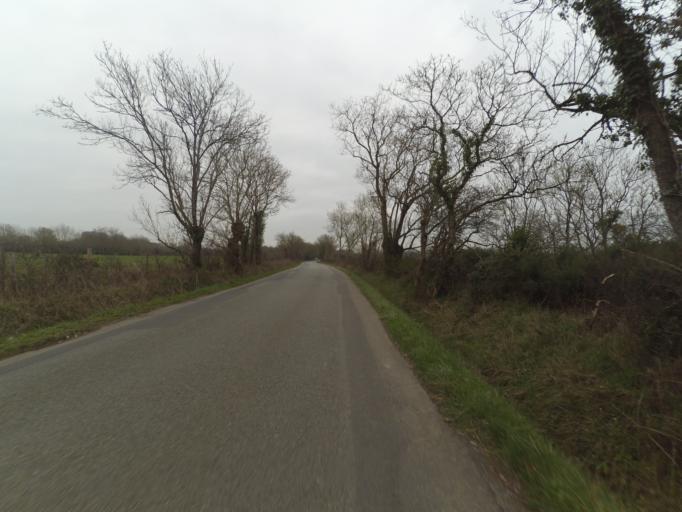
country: FR
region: Pays de la Loire
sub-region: Departement de la Loire-Atlantique
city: Indre
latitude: 47.2289
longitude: -1.6861
